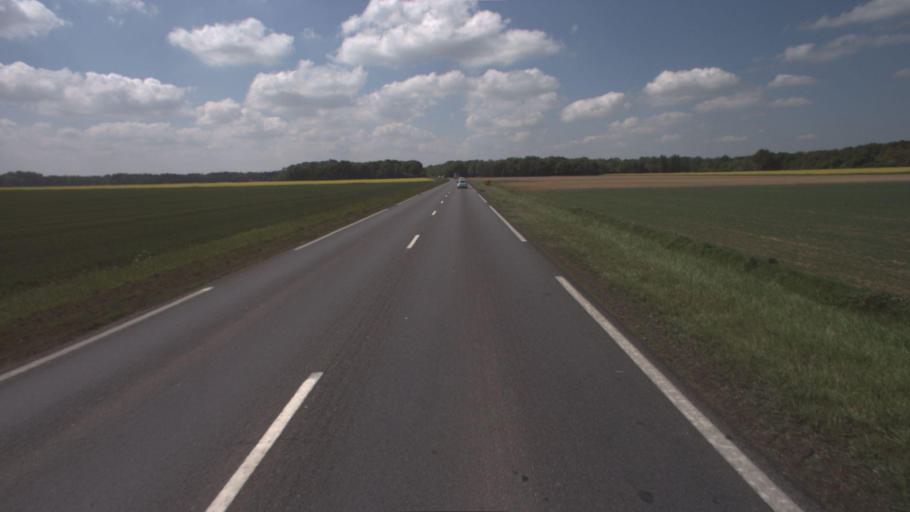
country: FR
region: Ile-de-France
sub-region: Departement de Seine-et-Marne
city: Chaumes-en-Brie
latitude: 48.7024
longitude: 2.8302
